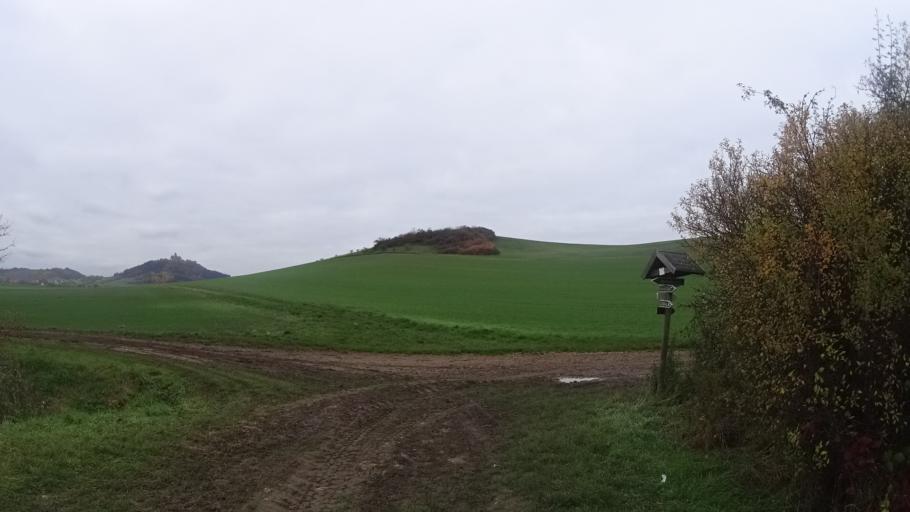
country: DE
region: Thuringia
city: Arnstadt
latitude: 50.8545
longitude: 10.9050
